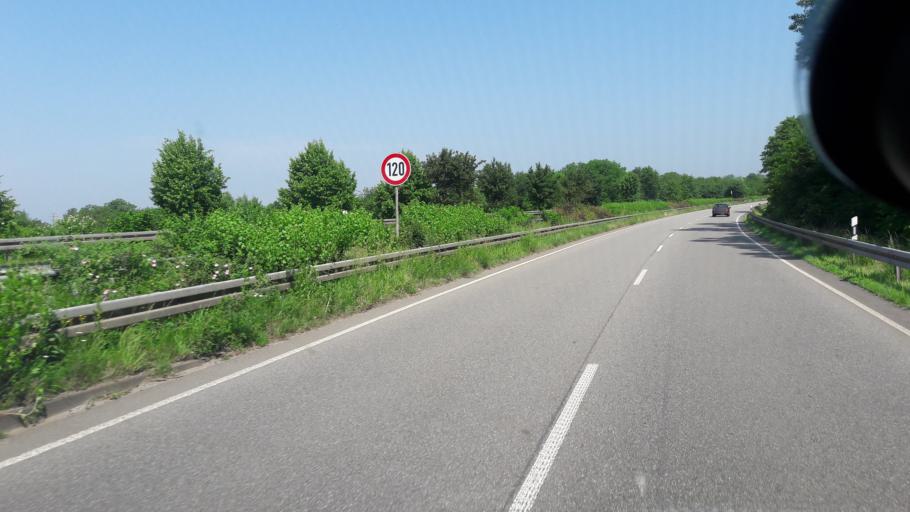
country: DE
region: Baden-Wuerttemberg
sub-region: Karlsruhe Region
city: Bischweier
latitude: 48.8341
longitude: 8.2688
